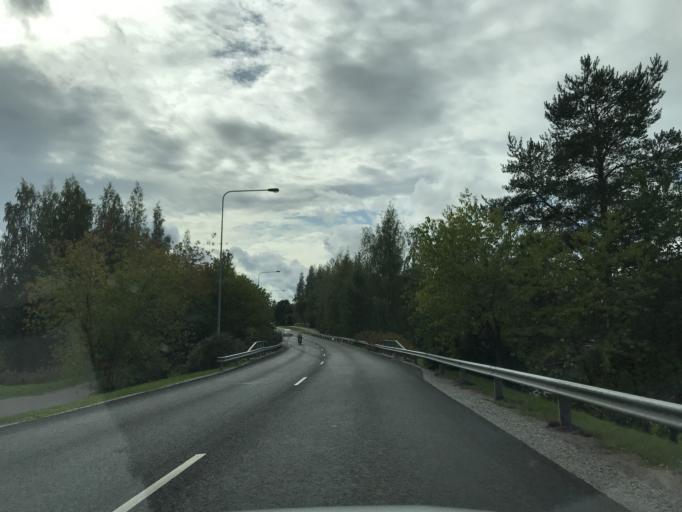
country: FI
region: Paijanne Tavastia
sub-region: Lahti
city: Lahti
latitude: 61.0086
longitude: 25.7798
